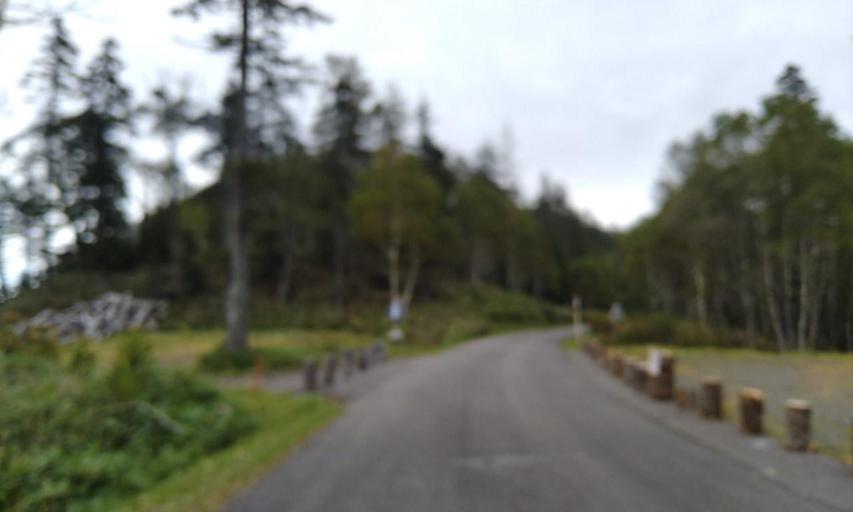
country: JP
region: Hokkaido
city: Bihoro
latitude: 43.5757
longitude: 144.2256
